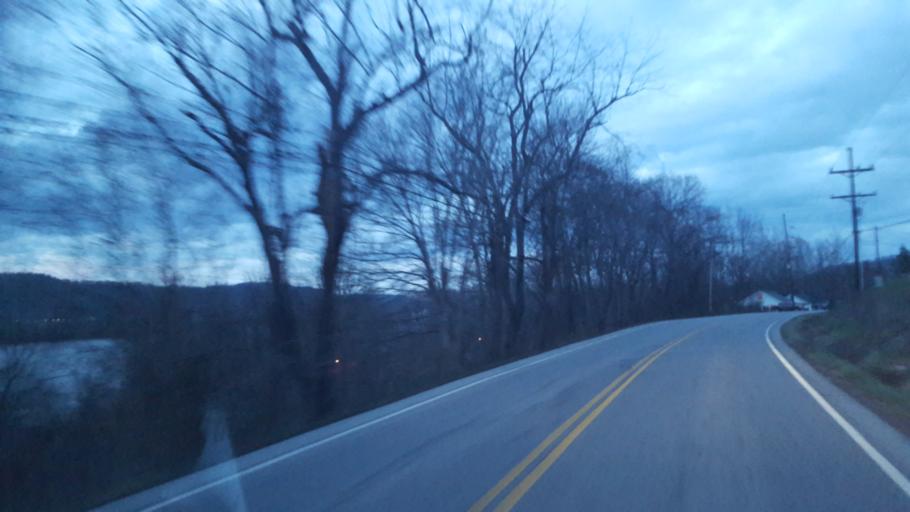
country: US
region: Ohio
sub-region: Scioto County
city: Portsmouth
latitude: 38.6934
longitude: -83.0481
